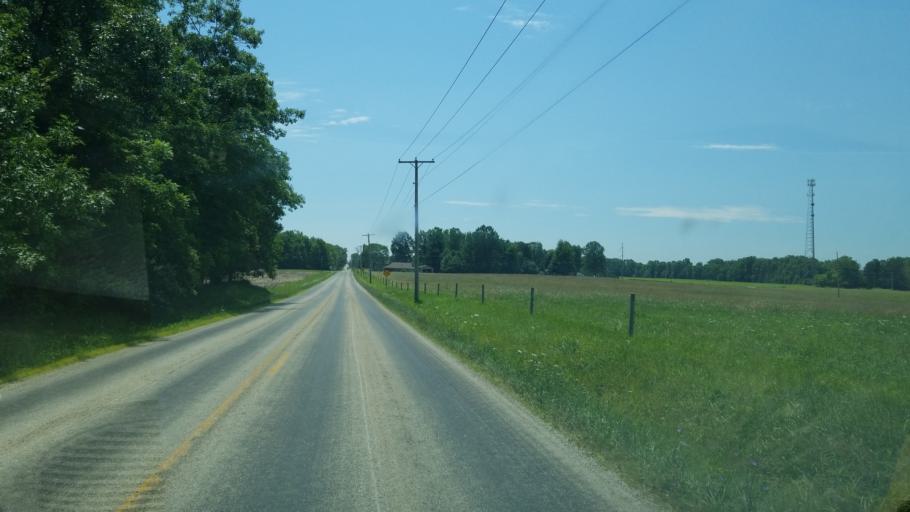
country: US
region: Ohio
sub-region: Ashland County
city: Ashland
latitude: 40.8689
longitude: -82.3491
